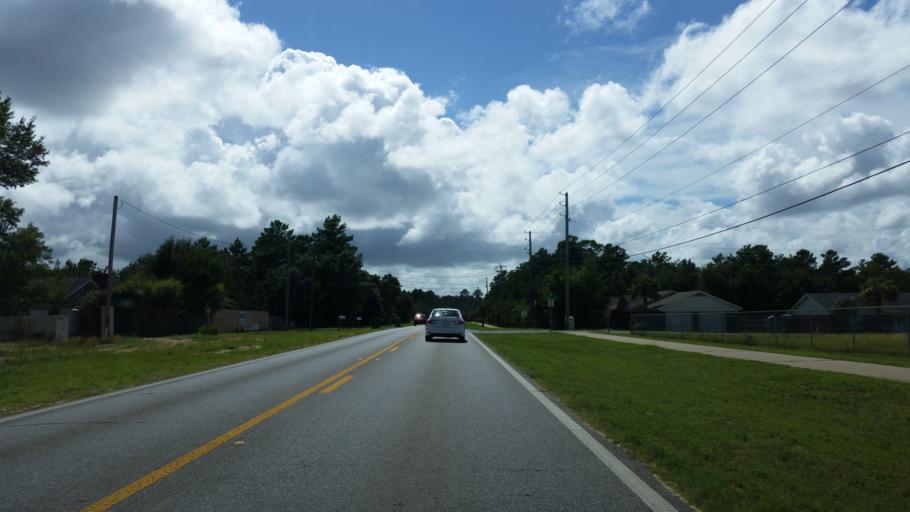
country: US
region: Florida
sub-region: Santa Rosa County
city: Holley
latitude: 30.4329
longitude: -86.9013
